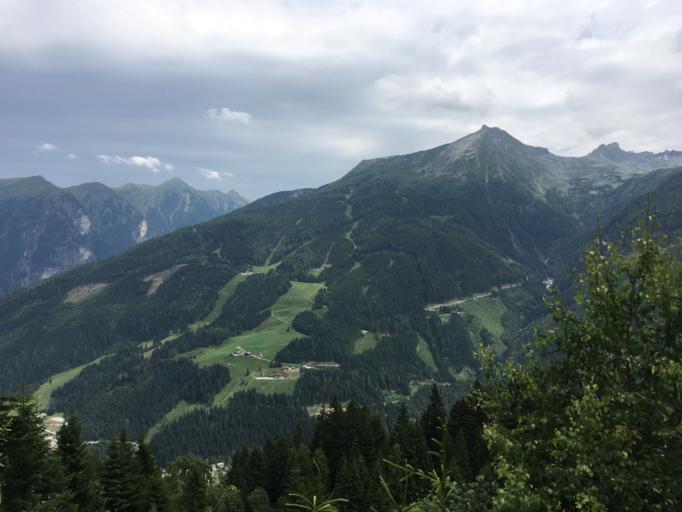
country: AT
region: Salzburg
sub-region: Politischer Bezirk Sankt Johann im Pongau
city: Bad Gastein
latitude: 47.1109
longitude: 13.1184
